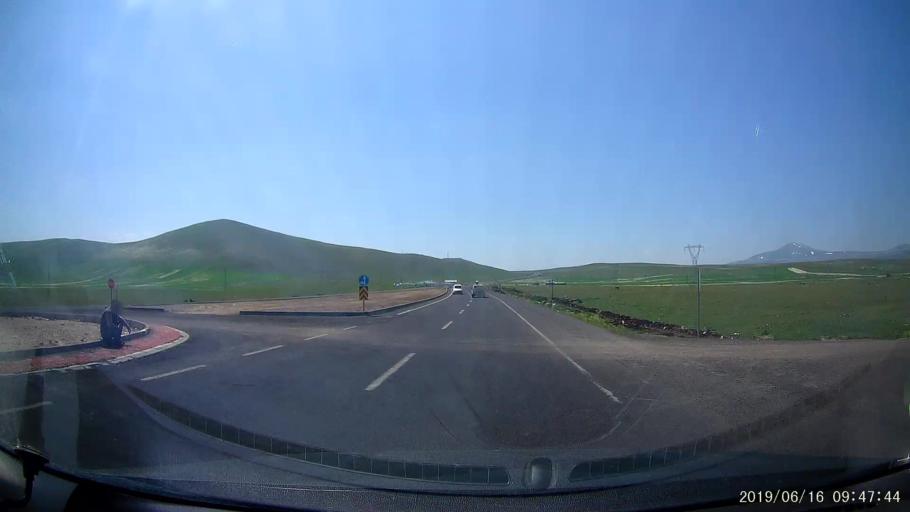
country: TR
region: Kars
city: Digor
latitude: 40.4420
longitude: 43.3474
